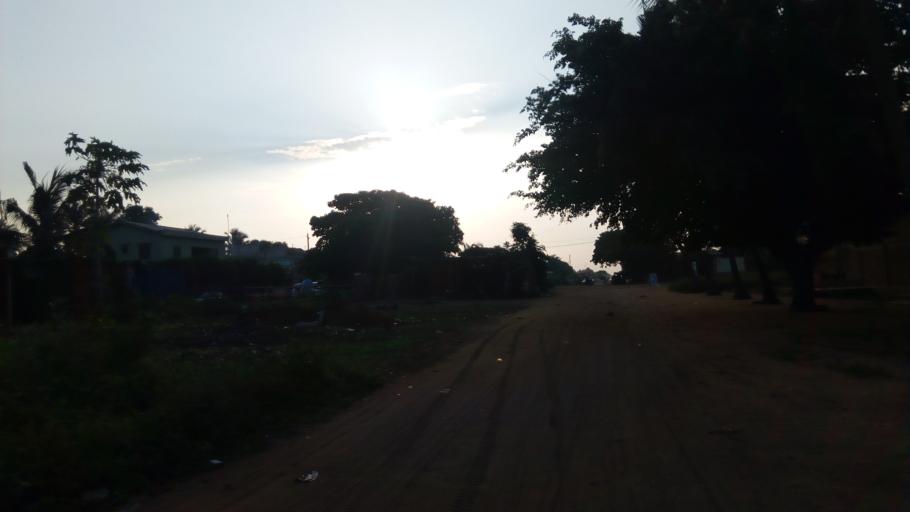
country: TG
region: Maritime
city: Lome
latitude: 6.1794
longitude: 1.1870
